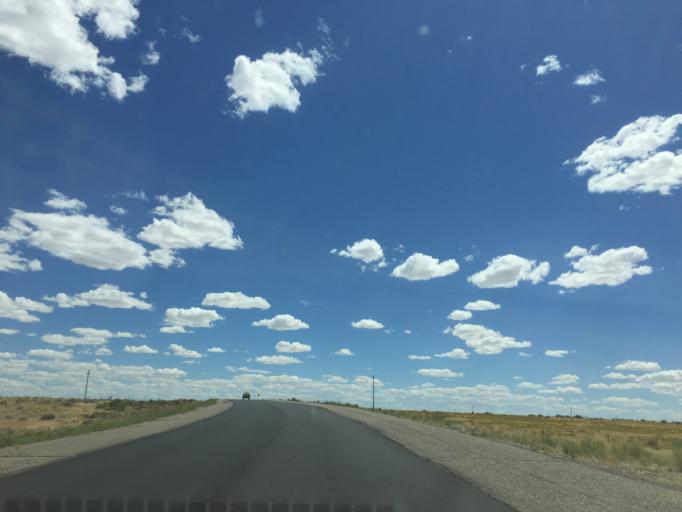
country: US
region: New Mexico
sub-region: San Juan County
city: Upper Fruitland
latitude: 36.4832
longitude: -108.2568
